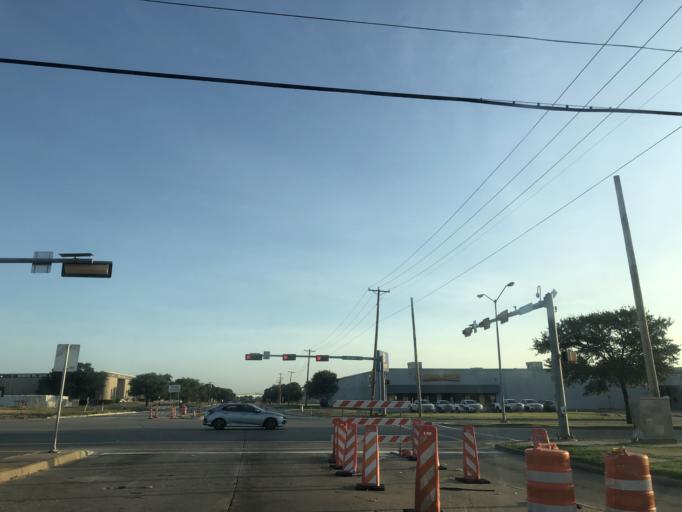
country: US
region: Texas
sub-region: Dallas County
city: Balch Springs
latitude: 32.7681
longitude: -96.6466
